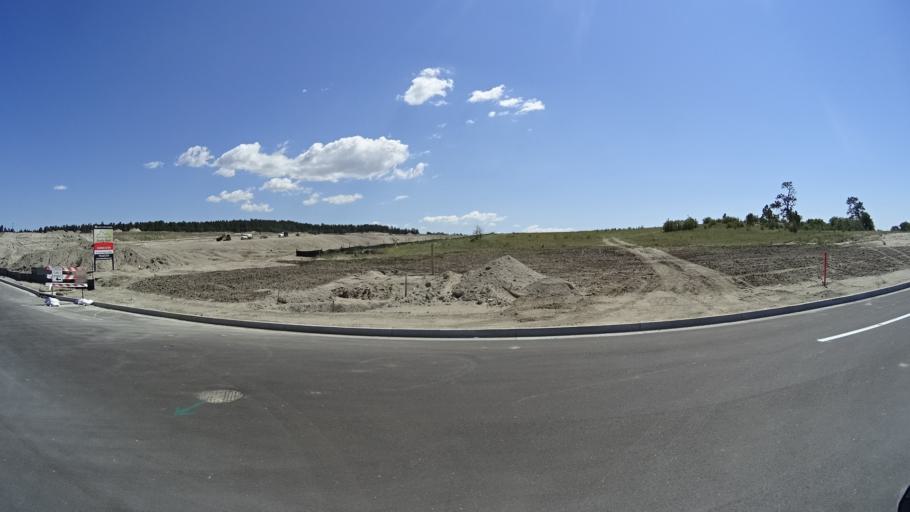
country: US
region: Colorado
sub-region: El Paso County
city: Black Forest
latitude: 38.9800
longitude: -104.7381
